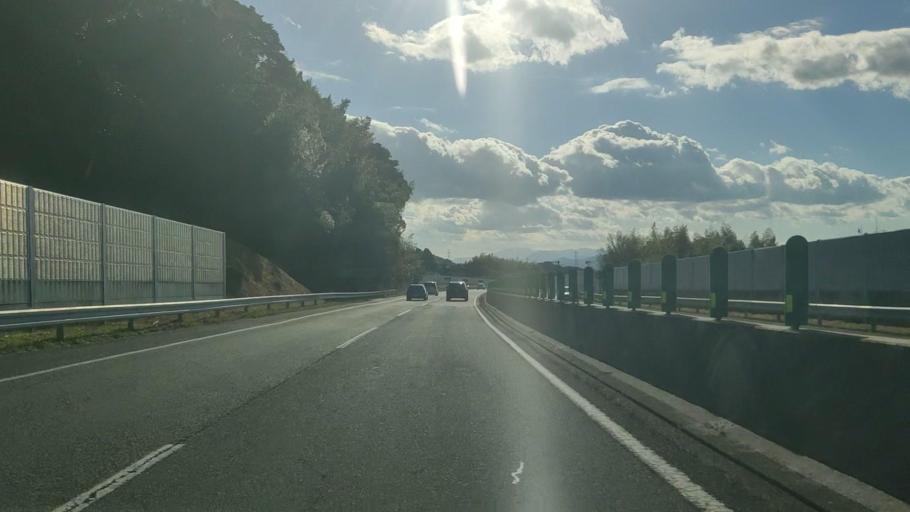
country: JP
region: Fukuoka
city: Nakama
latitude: 33.8274
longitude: 130.7645
